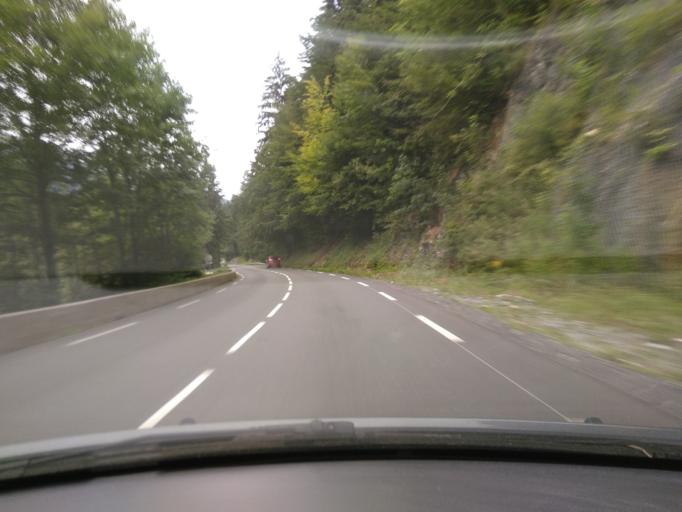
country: FR
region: Rhone-Alpes
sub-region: Departement de la Haute-Savoie
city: Saint-Jean-de-Sixt
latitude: 45.9438
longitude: 6.4030
